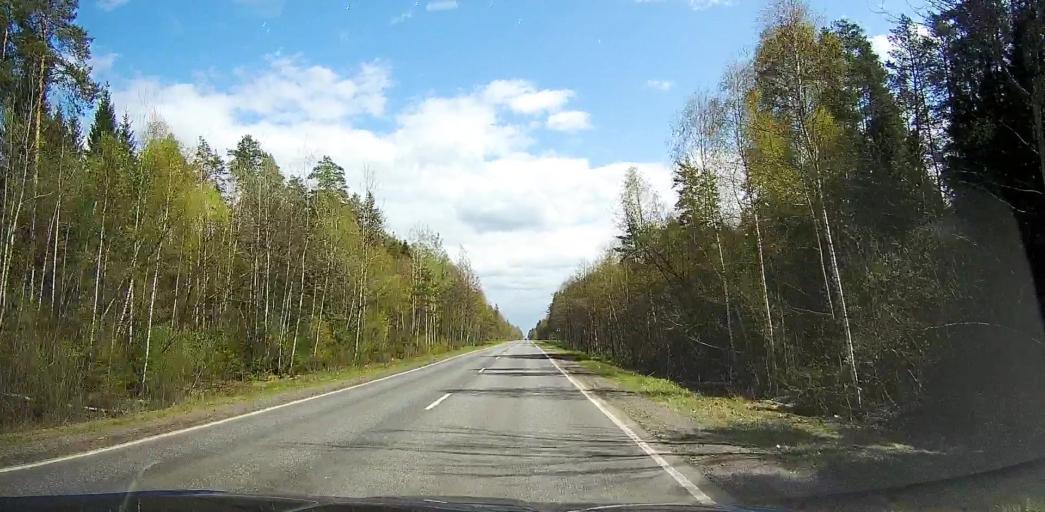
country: RU
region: Moskovskaya
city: Imeni Tsyurupy
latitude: 55.5515
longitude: 38.7279
